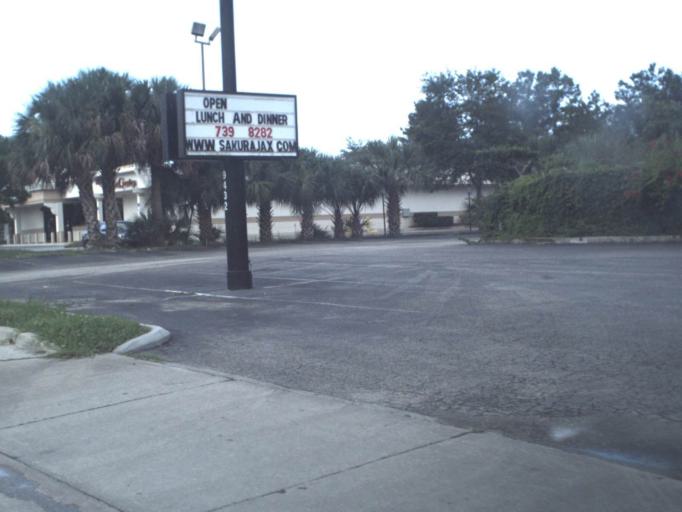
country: US
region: Florida
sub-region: Clay County
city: Orange Park
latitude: 30.2067
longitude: -81.6174
